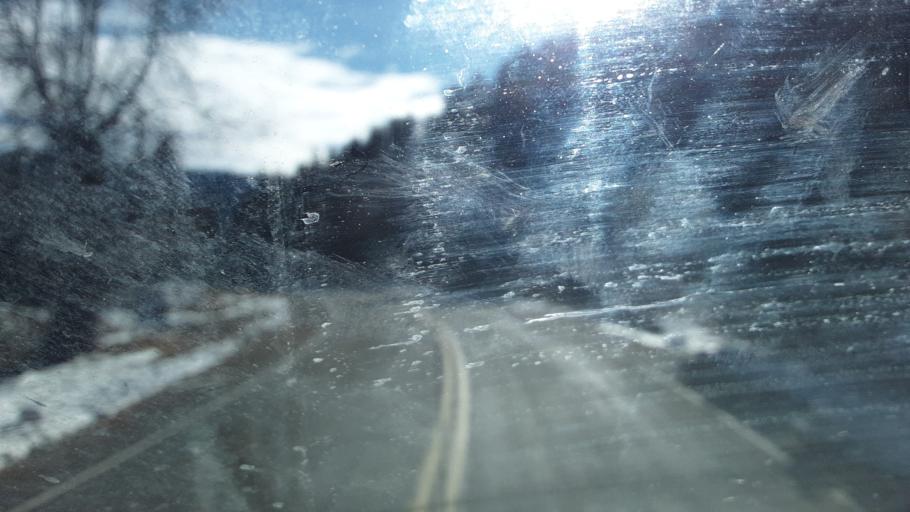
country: US
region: Colorado
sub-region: La Plata County
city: Bayfield
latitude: 37.3671
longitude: -107.6670
